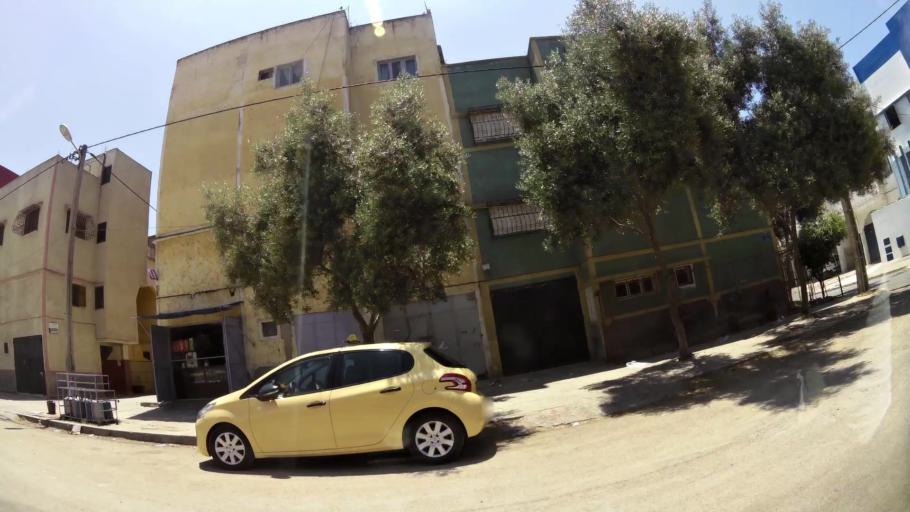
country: MA
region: Rabat-Sale-Zemmour-Zaer
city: Sale
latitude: 34.0649
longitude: -6.7930
